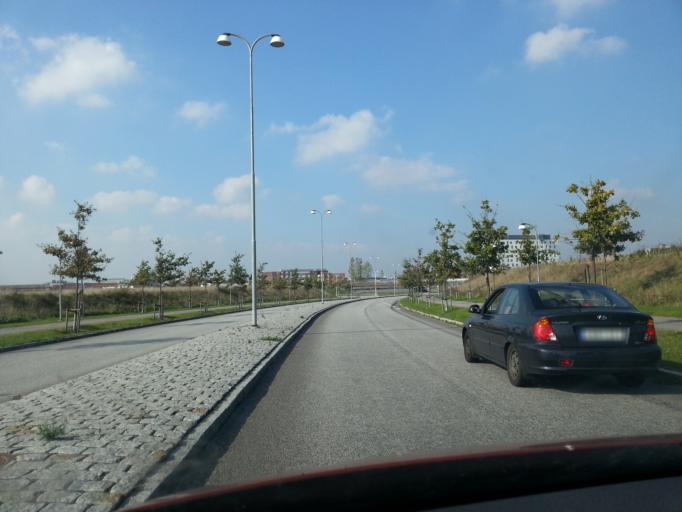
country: SE
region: Skane
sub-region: Lunds Kommun
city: Lund
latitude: 55.6852
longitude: 13.2025
